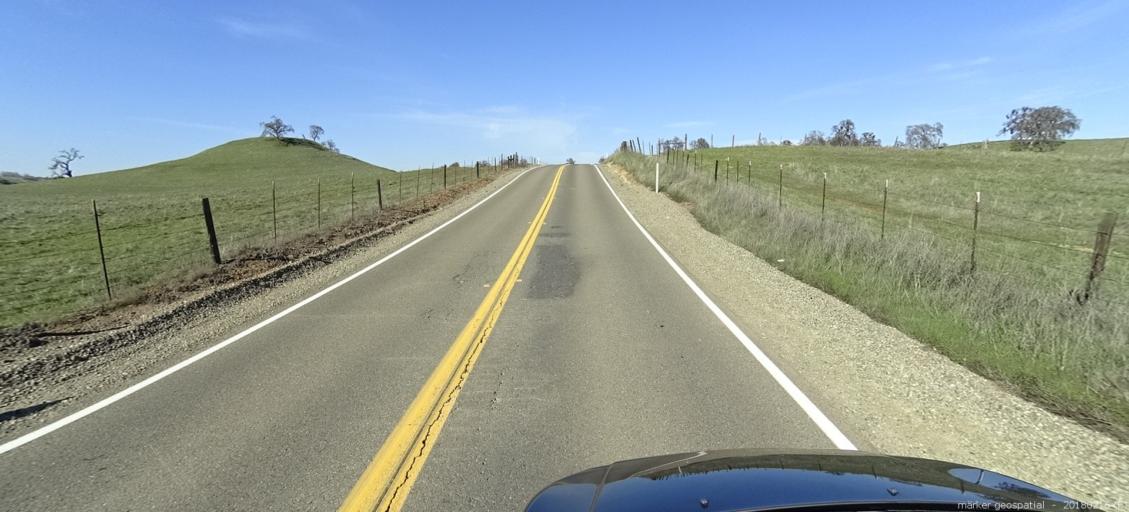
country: US
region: California
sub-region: Sacramento County
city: Rancho Murieta
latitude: 38.5829
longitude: -121.1305
